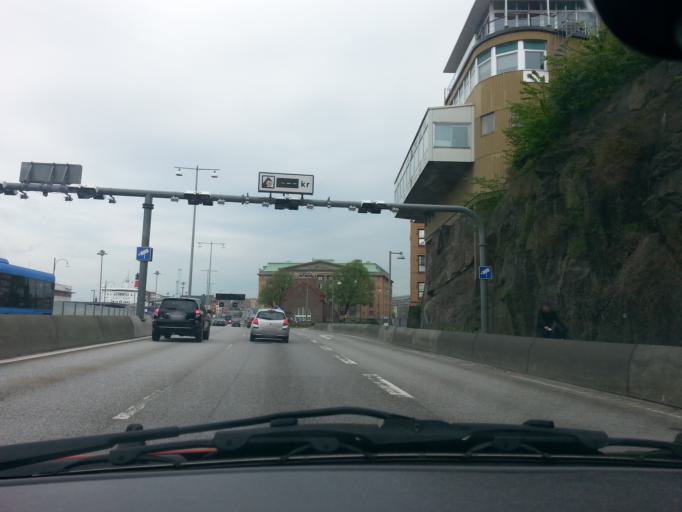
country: SE
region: Vaestra Goetaland
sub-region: Goteborg
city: Majorna
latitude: 57.6999
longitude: 11.9353
